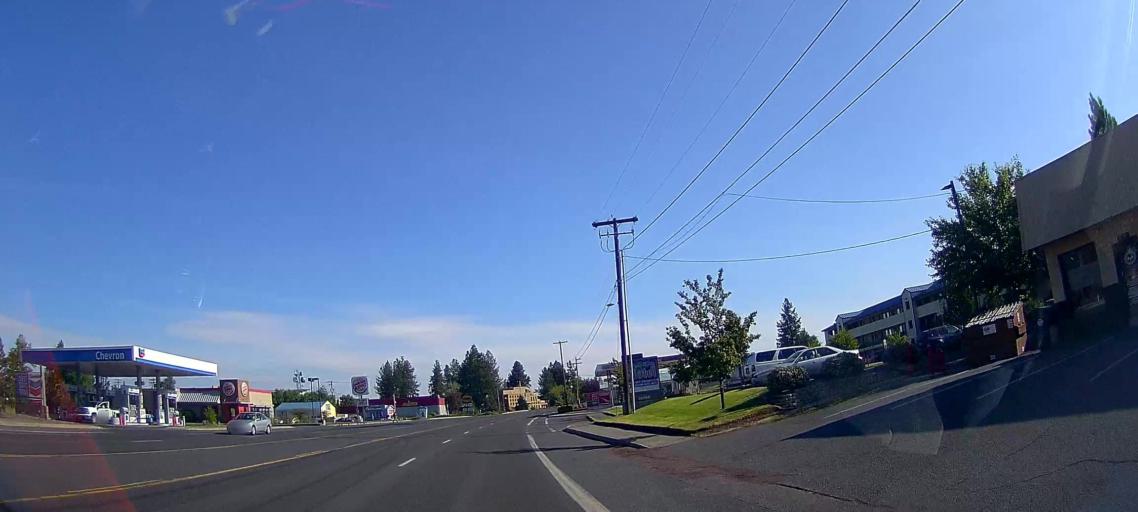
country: US
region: Oregon
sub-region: Deschutes County
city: Bend
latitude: 44.0858
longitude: -121.3059
